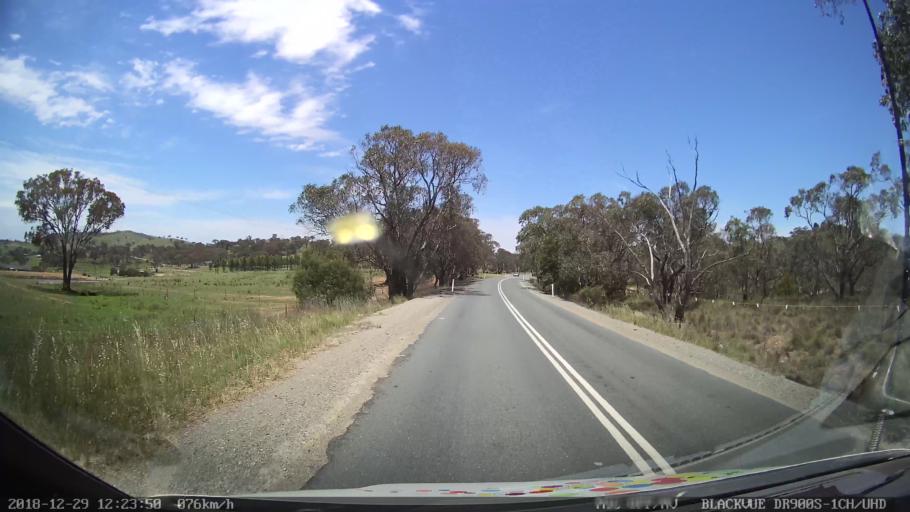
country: AU
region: New South Wales
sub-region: Queanbeyan
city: Queanbeyan
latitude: -35.4409
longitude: 149.2154
